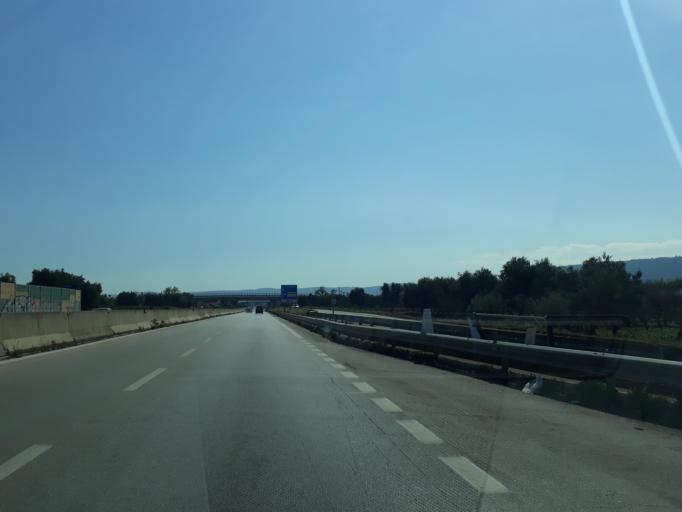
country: IT
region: Apulia
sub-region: Provincia di Brindisi
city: Fasano
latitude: 40.8760
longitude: 17.3404
